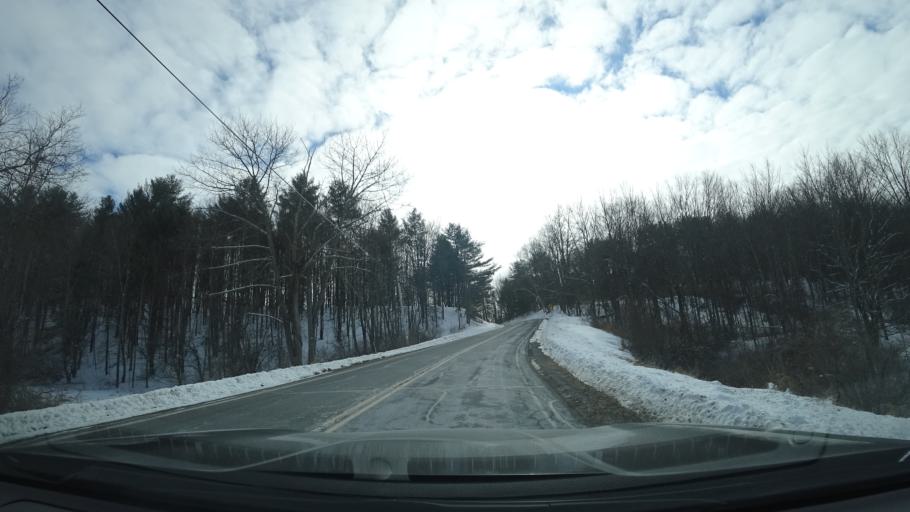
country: US
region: New York
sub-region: Washington County
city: Greenwich
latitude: 43.2428
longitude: -73.4058
